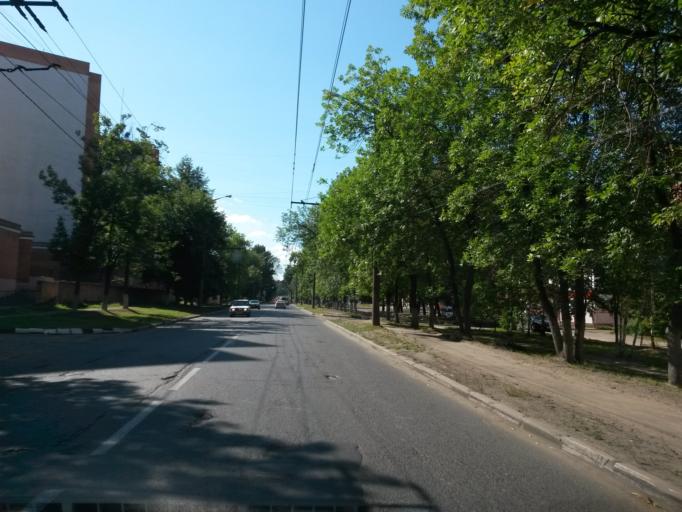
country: RU
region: Jaroslavl
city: Yaroslavl
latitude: 57.5832
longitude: 39.8384
